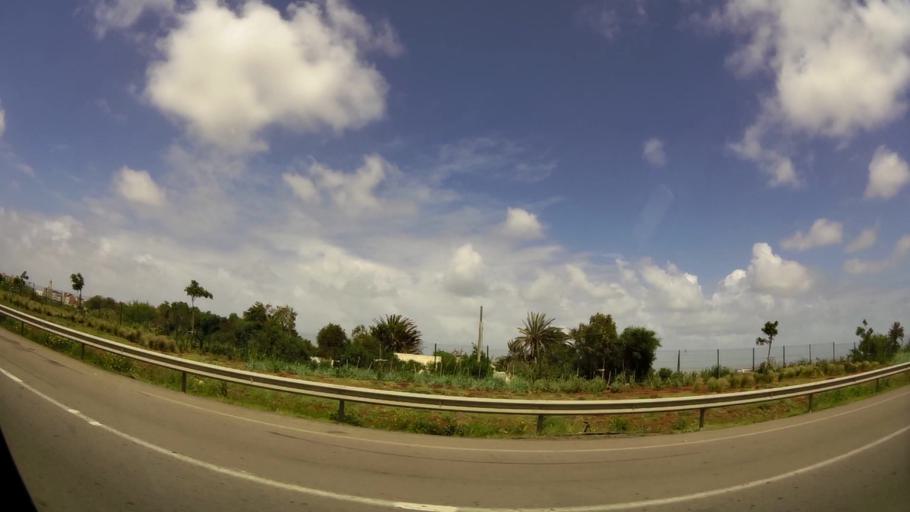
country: MA
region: Grand Casablanca
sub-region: Mediouna
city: Tit Mellil
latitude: 33.6222
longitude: -7.4701
